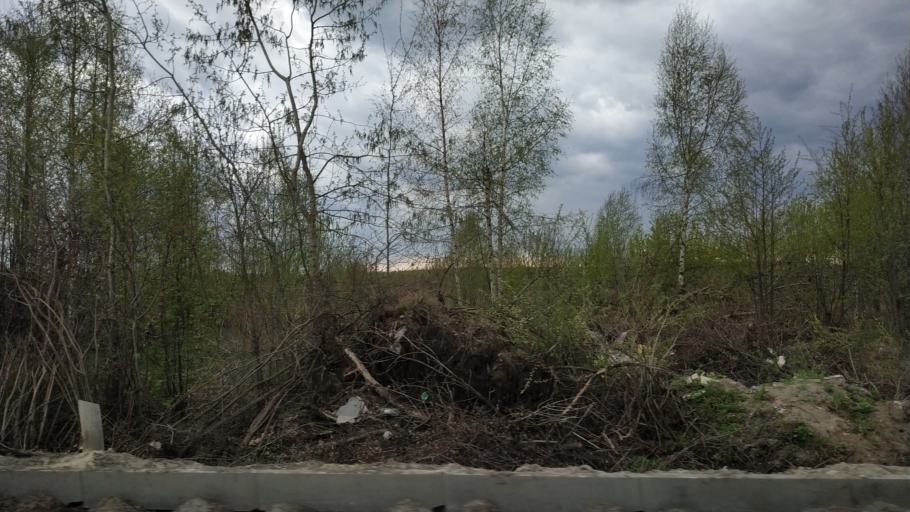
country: RU
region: Moskovskaya
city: Pavlovskiy Posad
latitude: 55.7990
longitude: 38.6868
